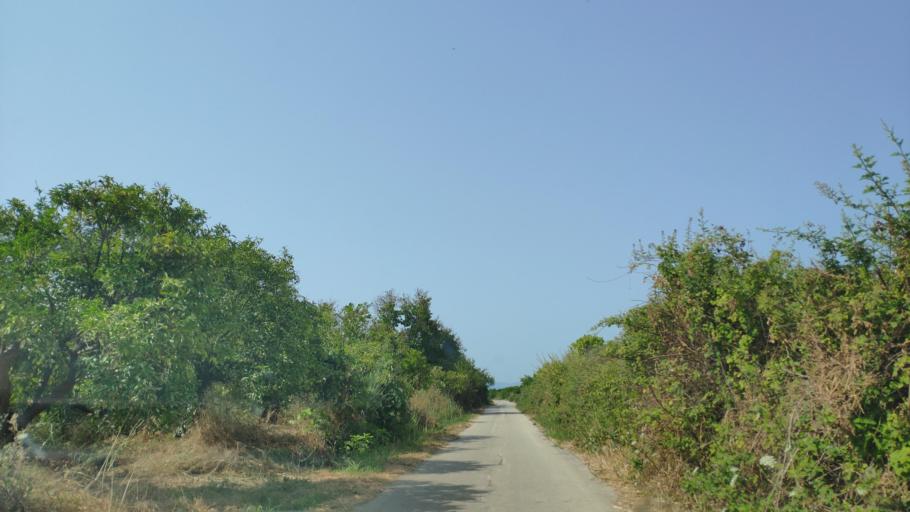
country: GR
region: Epirus
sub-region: Nomos Artas
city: Kompoti
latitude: 39.0616
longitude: 21.0742
